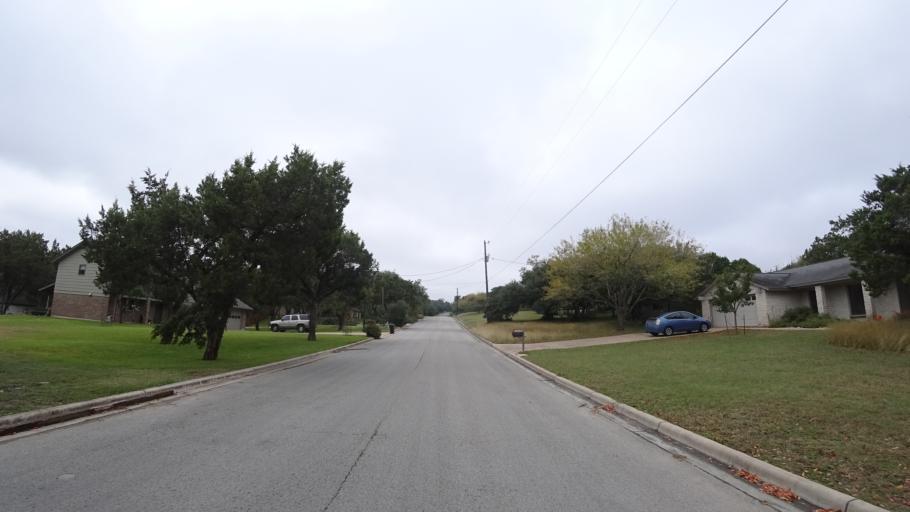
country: US
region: Texas
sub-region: Travis County
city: Barton Creek
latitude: 30.2256
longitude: -97.9052
